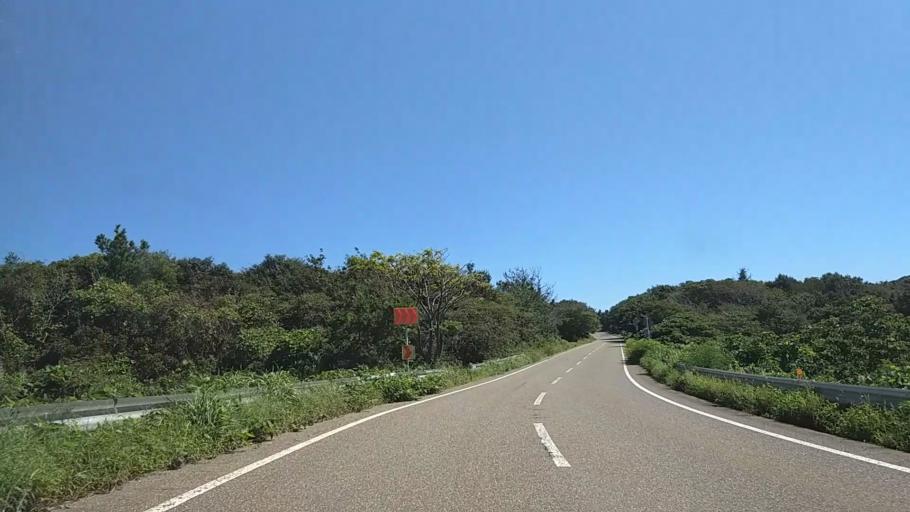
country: JP
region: Niigata
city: Joetsu
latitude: 37.1728
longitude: 138.1015
